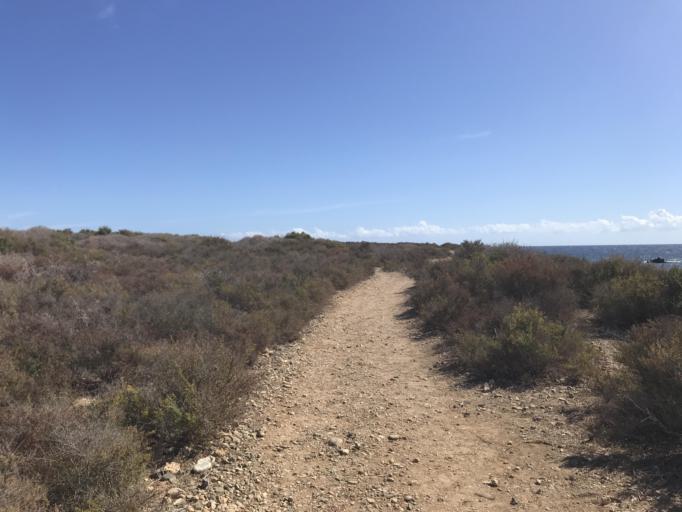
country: ES
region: Valencia
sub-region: Provincia de Alicante
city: Santa Pola
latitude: 38.1631
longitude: -0.4718
